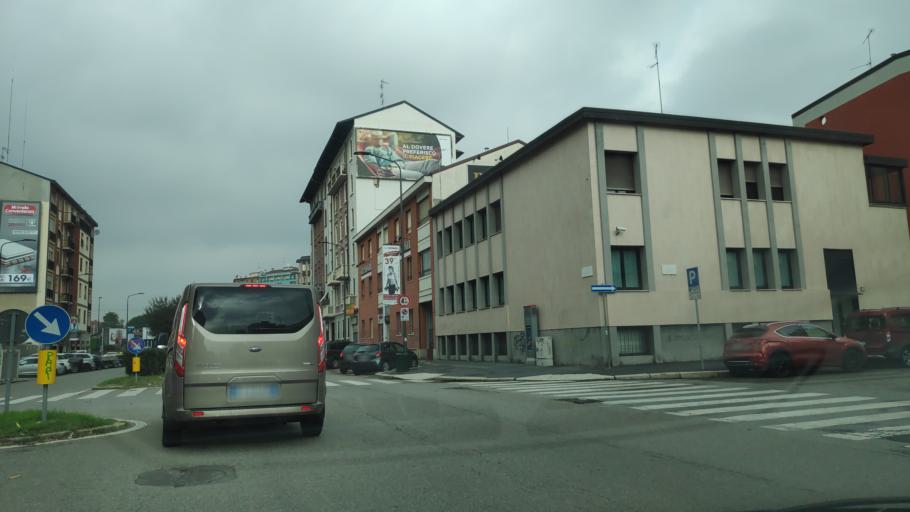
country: IT
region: Lombardy
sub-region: Citta metropolitana di Milano
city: Milano
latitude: 45.4418
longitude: 9.1727
